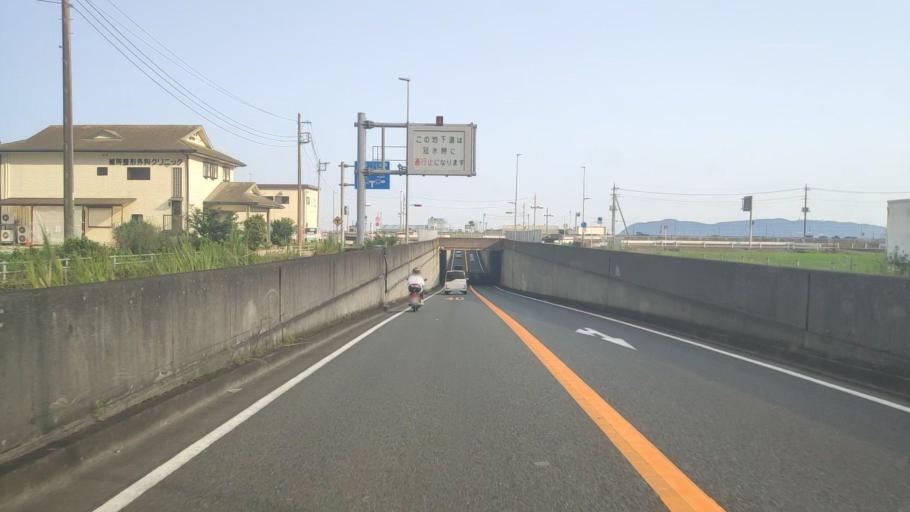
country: JP
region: Kanagawa
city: Isehara
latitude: 35.3752
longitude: 139.3196
